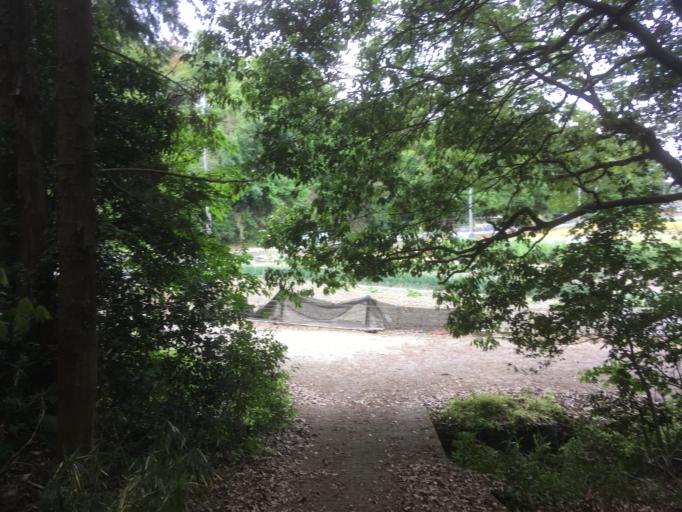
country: JP
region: Nara
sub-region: Ikoma-shi
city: Ikoma
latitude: 34.7063
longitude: 135.6727
